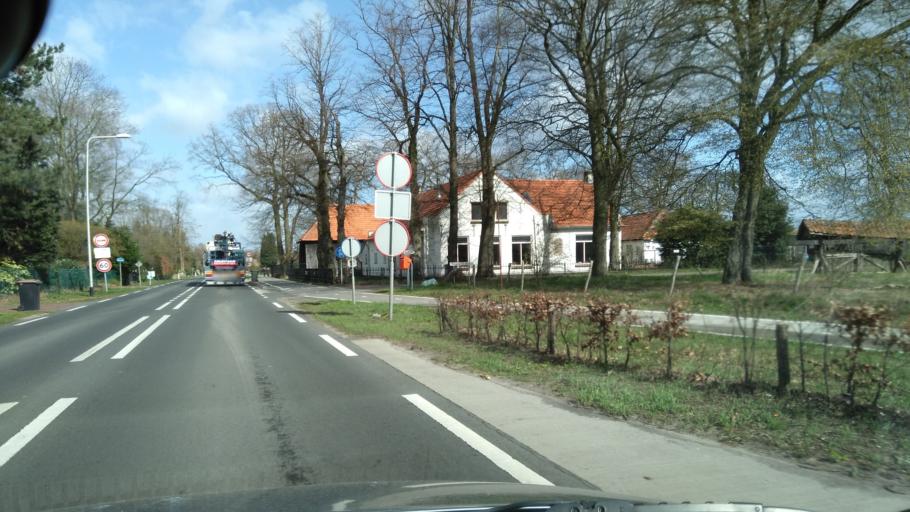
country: NL
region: North Brabant
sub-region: Gemeente Baarle-Nassau
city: Baarle-Nassau
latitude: 51.4051
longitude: 4.9365
